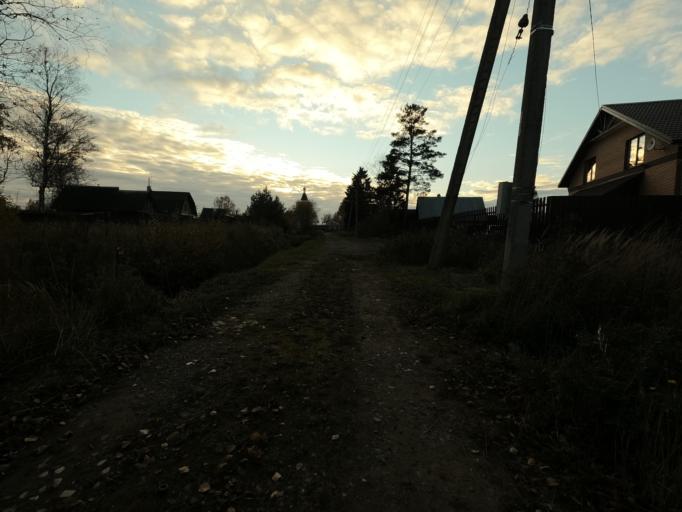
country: RU
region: Leningrad
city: Mga
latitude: 59.7750
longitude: 31.2158
